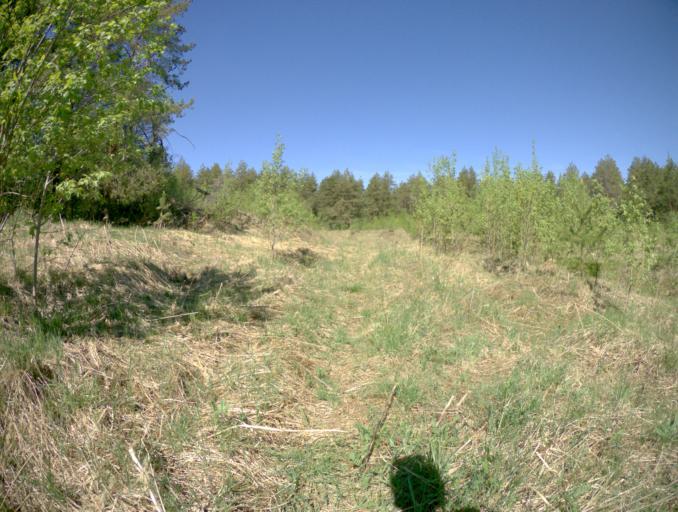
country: RU
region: Ivanovo
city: Gavrilov Posad
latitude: 56.4273
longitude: 40.2013
